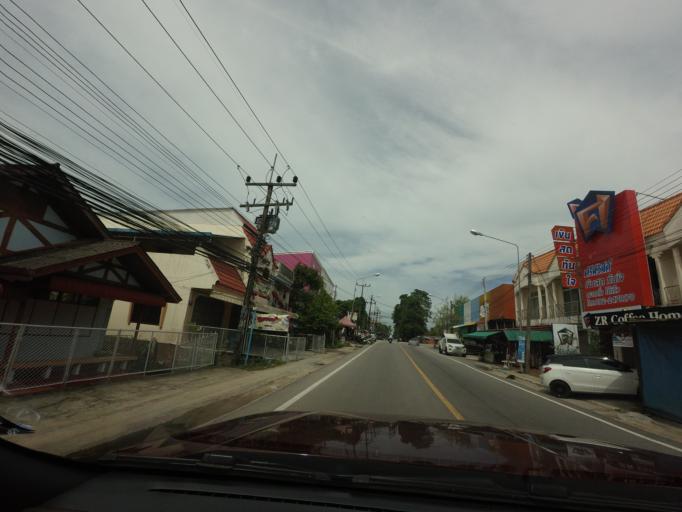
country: TH
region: Narathiwat
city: Tak Bai
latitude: 6.2564
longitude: 102.0504
